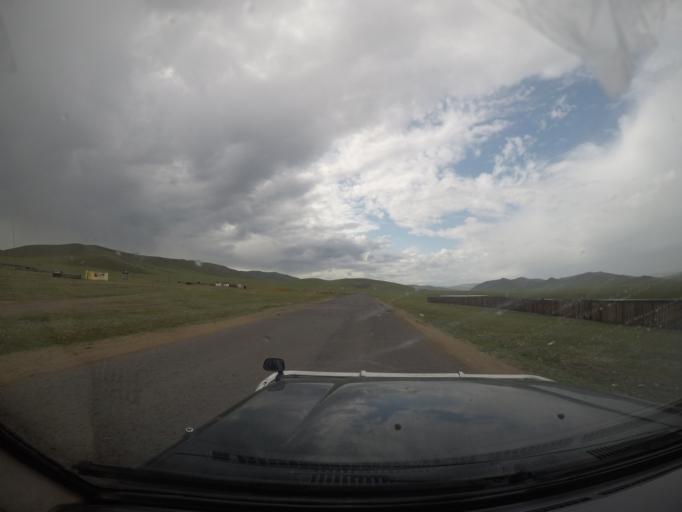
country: MN
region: Hentiy
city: Modot
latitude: 47.7324
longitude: 109.0089
